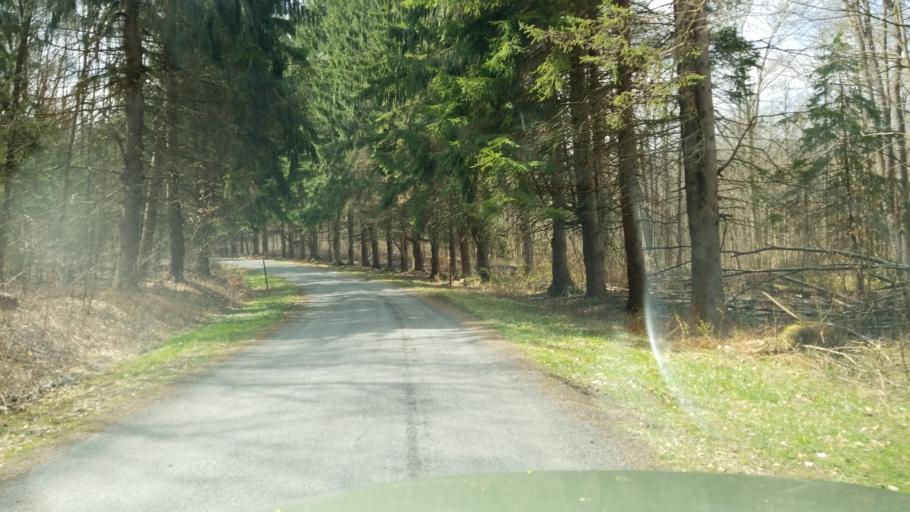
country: US
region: Pennsylvania
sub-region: Jefferson County
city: Brockway
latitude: 41.2876
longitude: -78.8759
